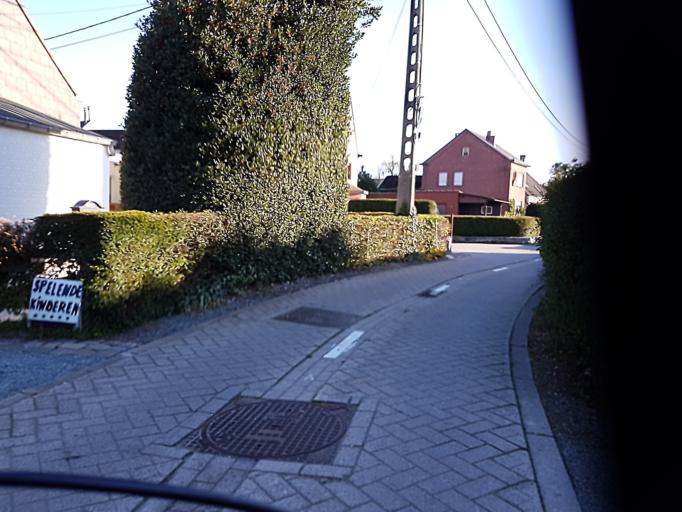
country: BE
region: Flanders
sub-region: Provincie Antwerpen
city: Bonheiden
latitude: 51.0380
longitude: 4.5340
